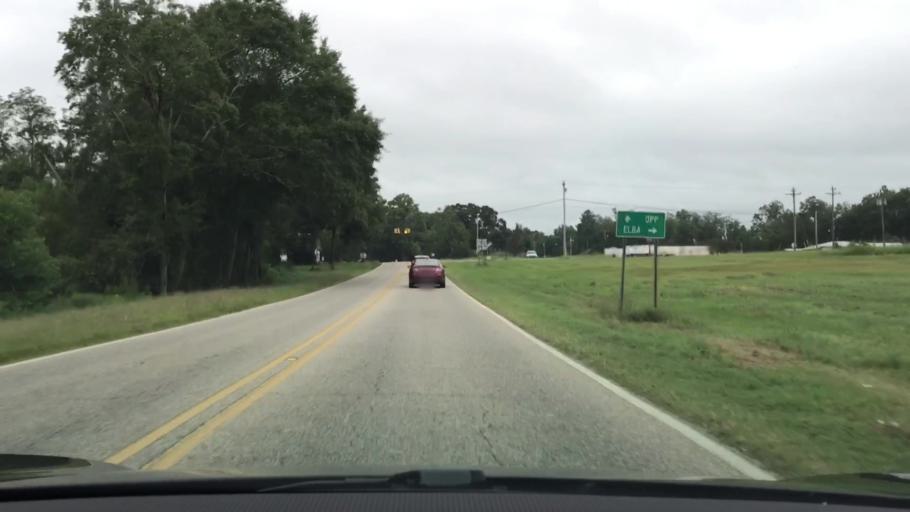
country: US
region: Alabama
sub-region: Covington County
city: Opp
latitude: 31.2146
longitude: -86.1698
